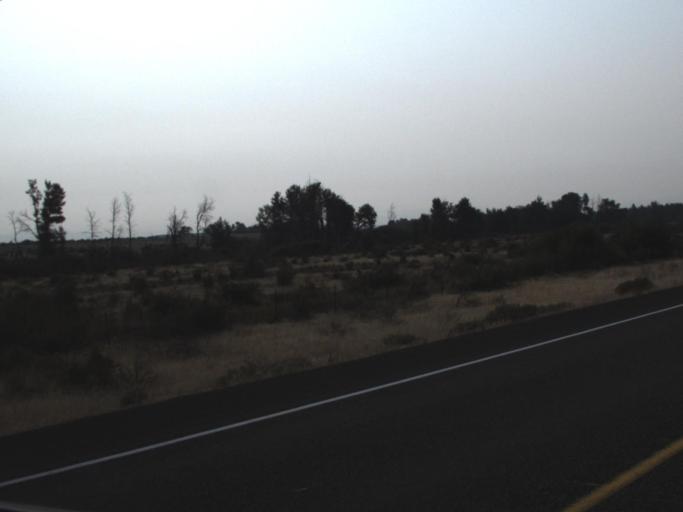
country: US
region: Washington
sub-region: Kittitas County
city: Ellensburg
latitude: 47.0946
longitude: -120.6569
